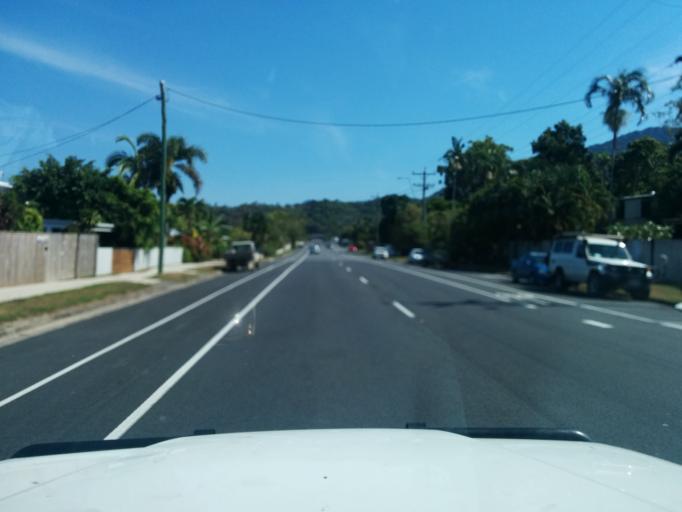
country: AU
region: Queensland
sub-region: Cairns
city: Redlynch
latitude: -16.9055
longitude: 145.7286
